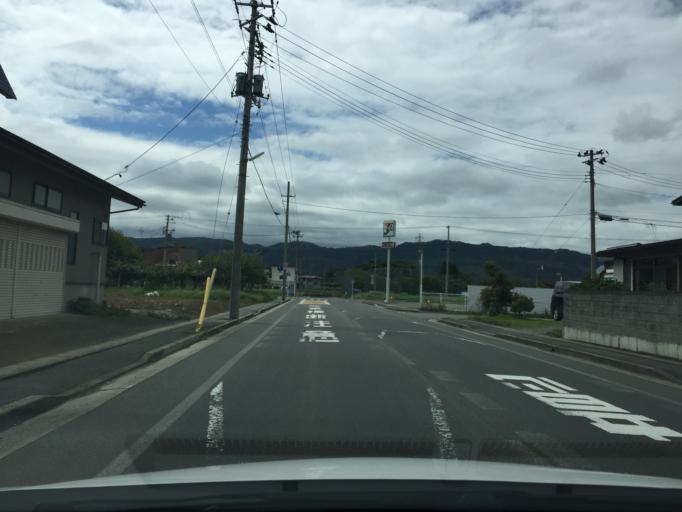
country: JP
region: Yamagata
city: Yonezawa
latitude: 37.8885
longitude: 140.1297
